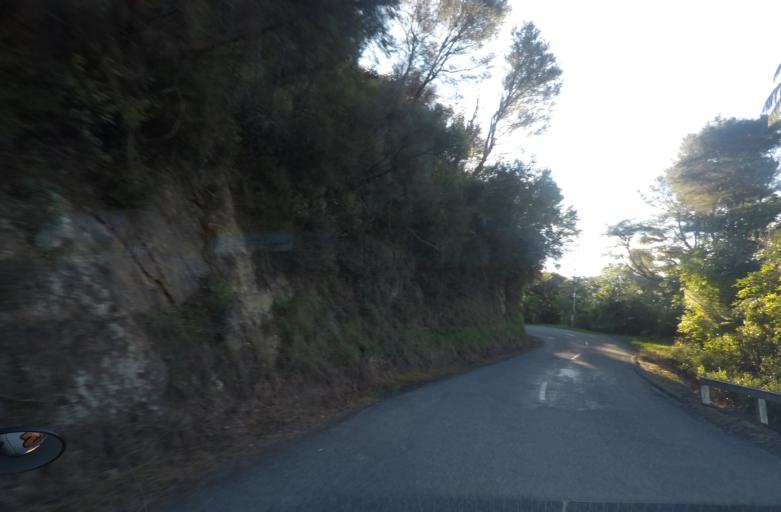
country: NZ
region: Marlborough
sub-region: Marlborough District
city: Picton
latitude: -41.2693
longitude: 173.9537
